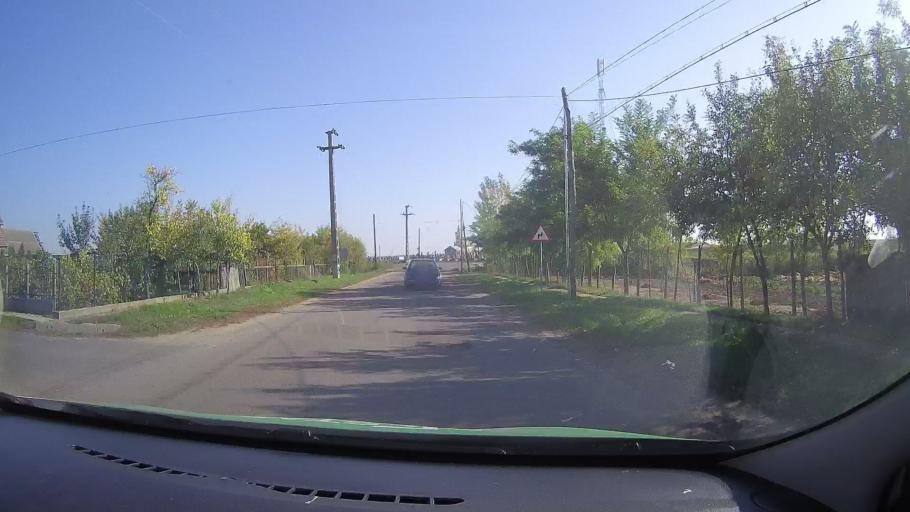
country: RO
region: Satu Mare
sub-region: Comuna Sanislau
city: Sanislau
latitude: 47.6424
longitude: 22.3329
